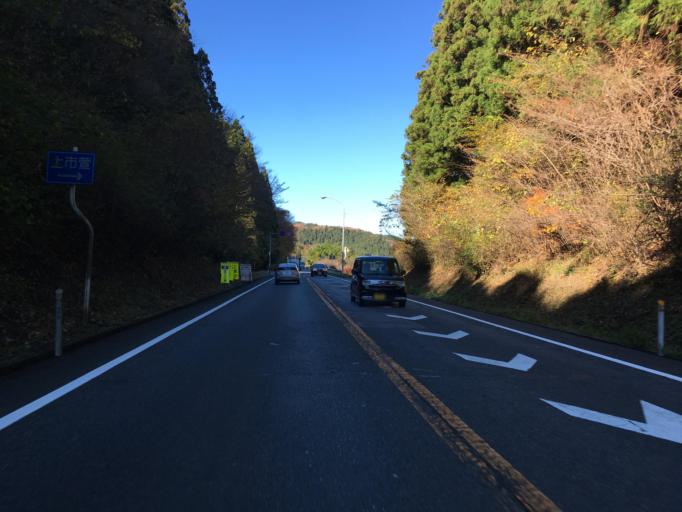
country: JP
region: Fukushima
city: Ishikawa
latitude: 37.1484
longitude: 140.6659
